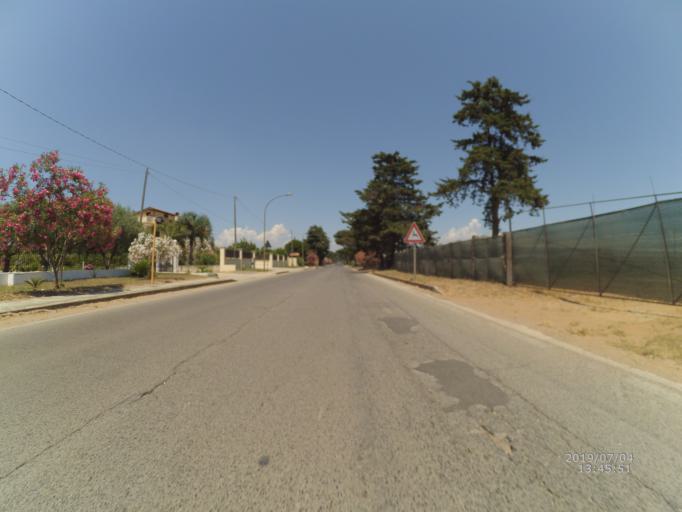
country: IT
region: Latium
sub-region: Provincia di Latina
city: San Felice Circeo
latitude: 41.2664
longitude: 13.0953
